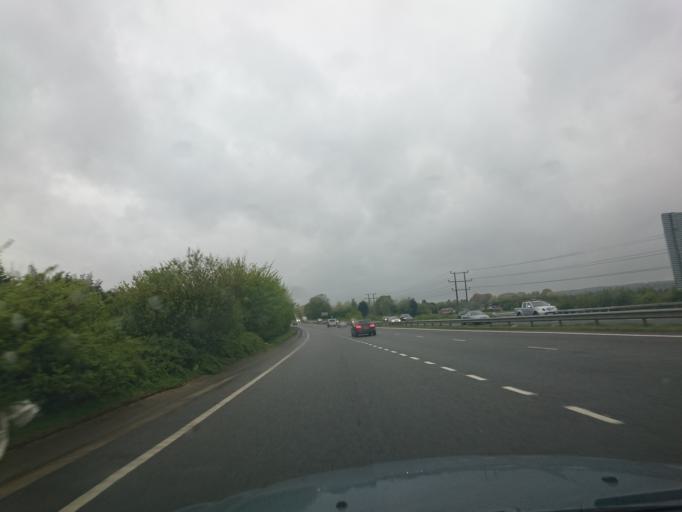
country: GB
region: England
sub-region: Hampshire
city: Aldershot
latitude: 51.2265
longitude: -0.7488
